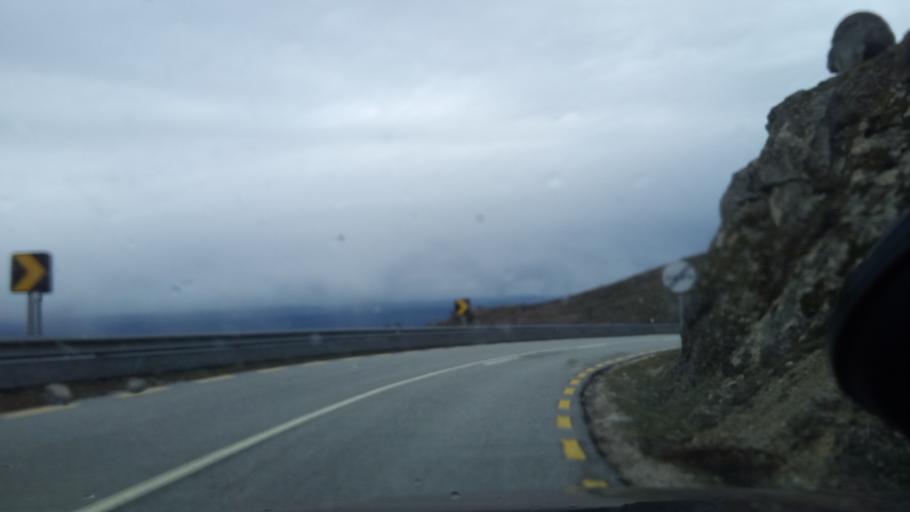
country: PT
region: Guarda
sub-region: Manteigas
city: Manteigas
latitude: 40.4459
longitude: -7.6019
